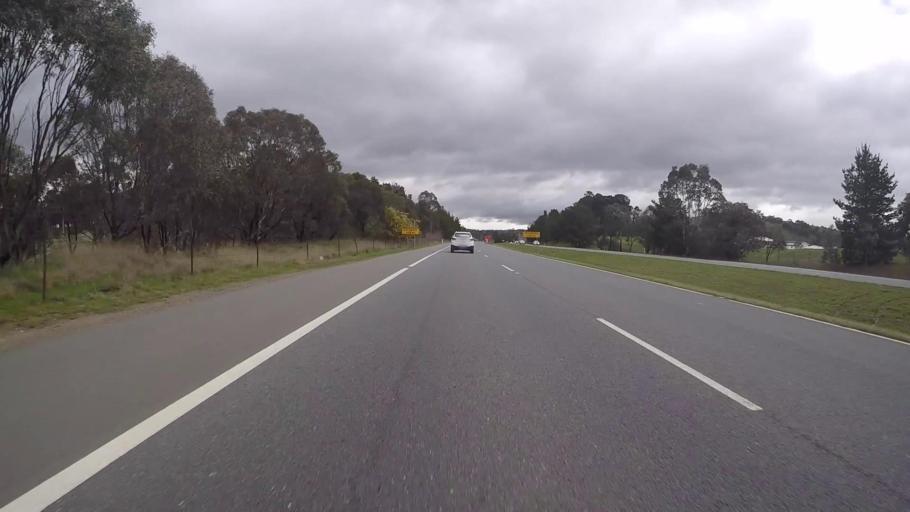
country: AU
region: Australian Capital Territory
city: Kaleen
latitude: -35.2053
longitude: 149.0999
